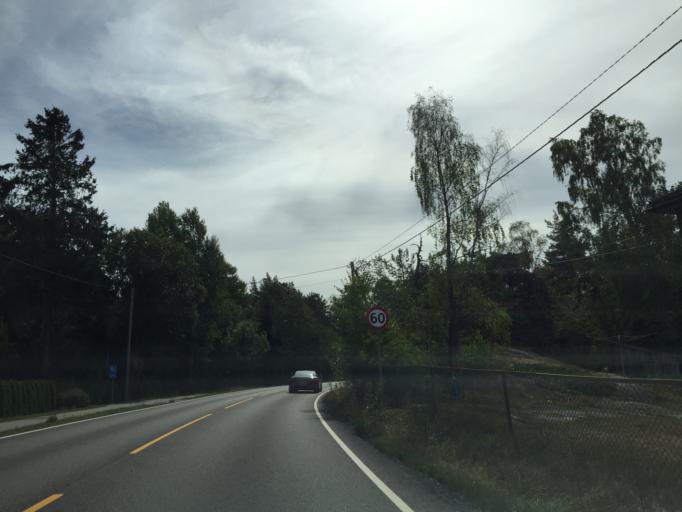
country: NO
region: Ostfold
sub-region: Fredrikstad
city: Fredrikstad
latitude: 59.1559
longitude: 10.9343
